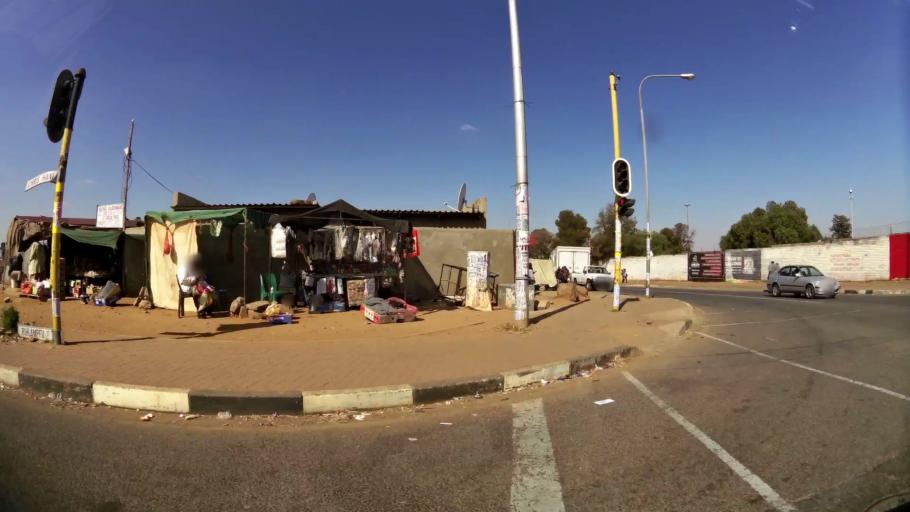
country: ZA
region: Gauteng
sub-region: City of Johannesburg Metropolitan Municipality
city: Soweto
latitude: -26.2783
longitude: 27.8646
